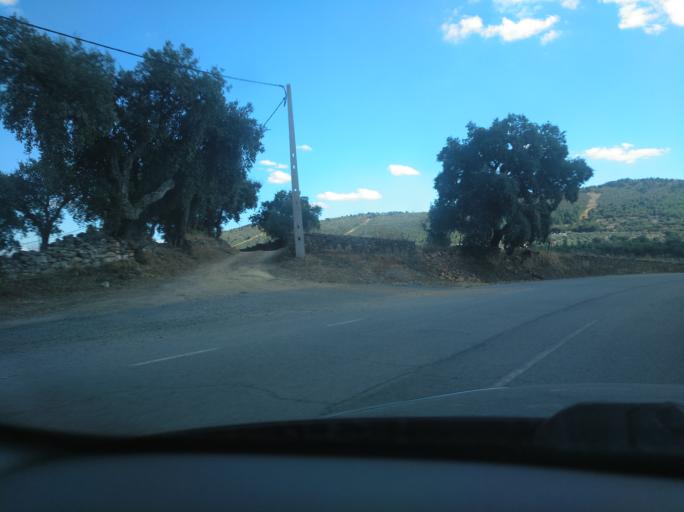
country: ES
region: Extremadura
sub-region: Provincia de Badajoz
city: La Codosera
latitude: 39.1630
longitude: -7.1863
